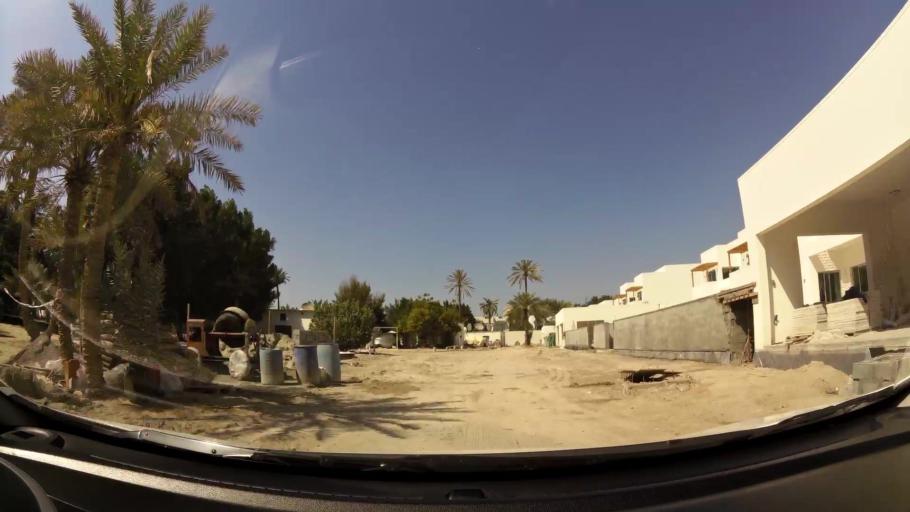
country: BH
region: Manama
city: Manama
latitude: 26.2173
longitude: 50.5837
